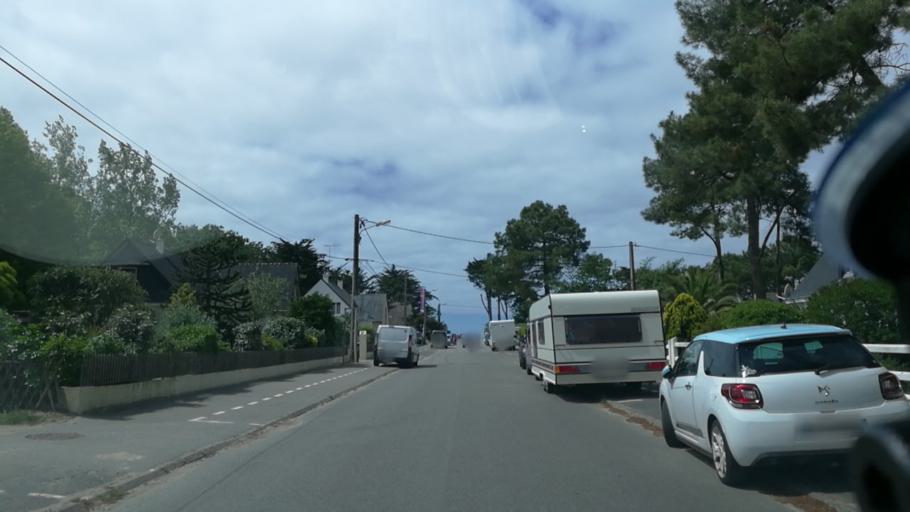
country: FR
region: Brittany
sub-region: Departement du Morbihan
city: Penestin
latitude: 47.4464
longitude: -2.4505
